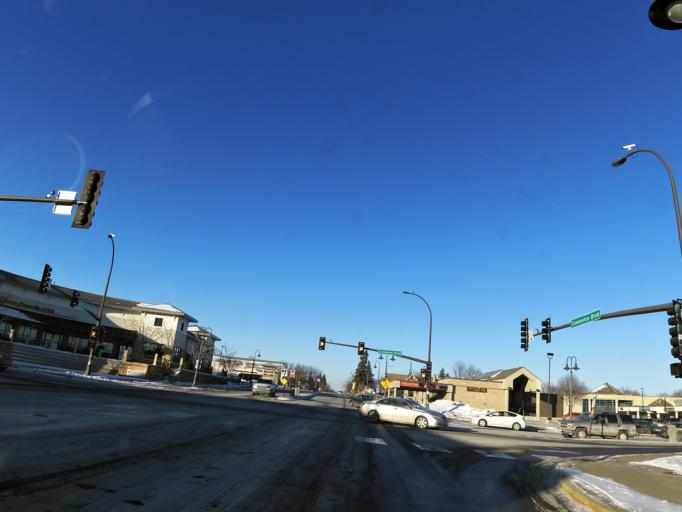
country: US
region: Minnesota
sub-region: Hennepin County
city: Mound
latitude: 44.9376
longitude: -93.6663
